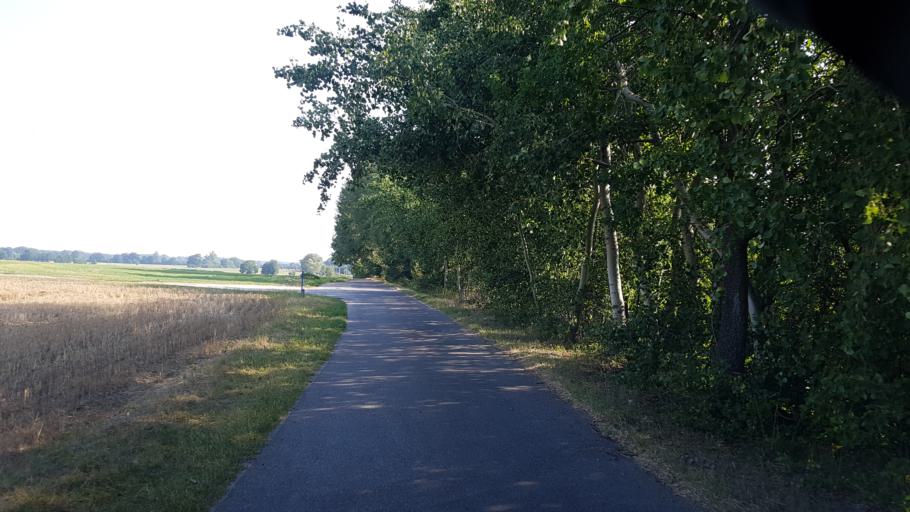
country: DE
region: Brandenburg
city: Drebkau
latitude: 51.6692
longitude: 14.2410
